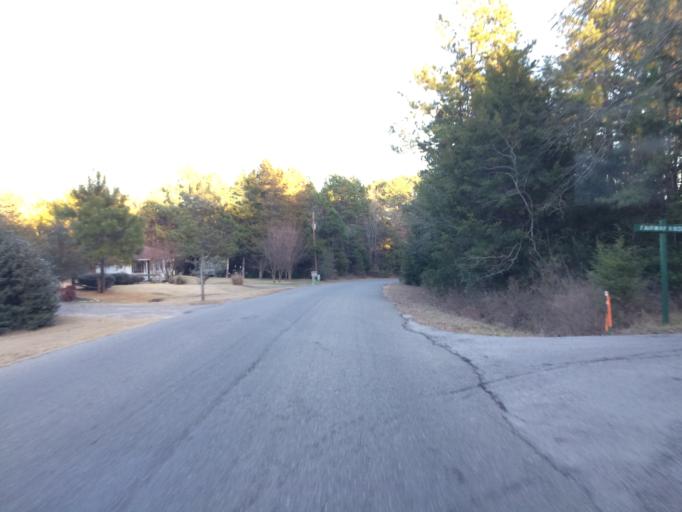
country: US
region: Texas
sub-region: Wood County
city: Hawkins
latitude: 32.7274
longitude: -95.1902
